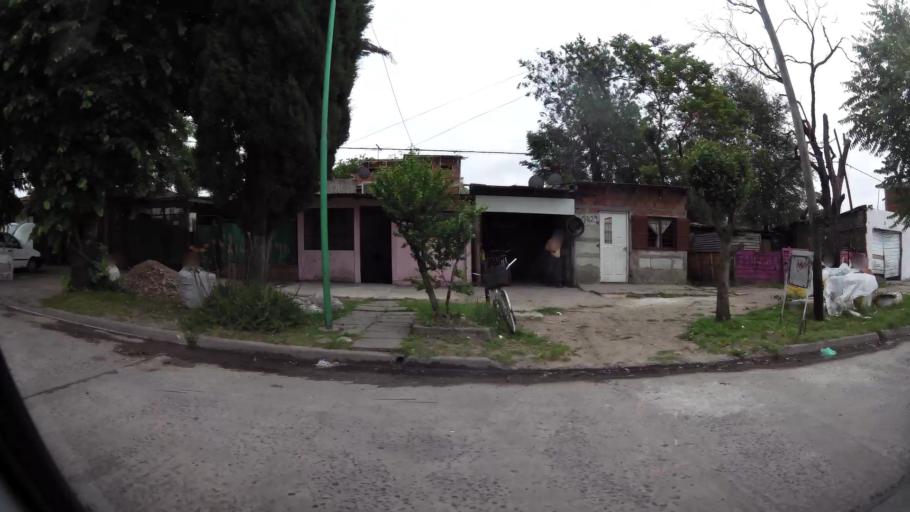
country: AR
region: Buenos Aires
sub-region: Partido de La Plata
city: La Plata
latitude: -34.9083
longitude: -57.9783
